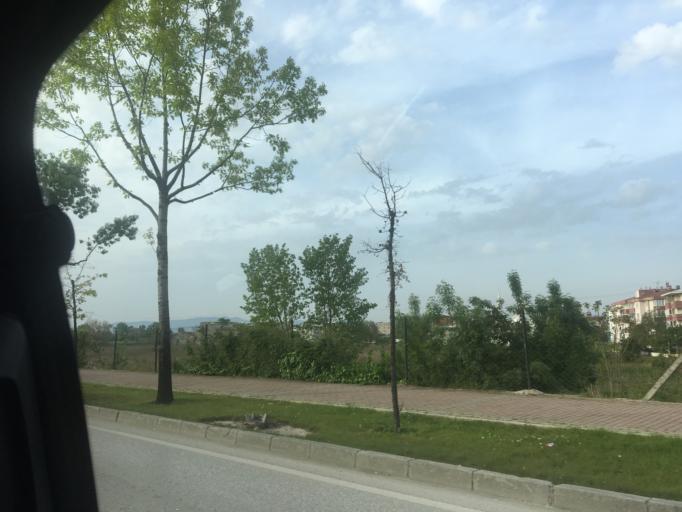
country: TR
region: Bursa
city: Yildirim
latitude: 40.2075
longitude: 29.0275
